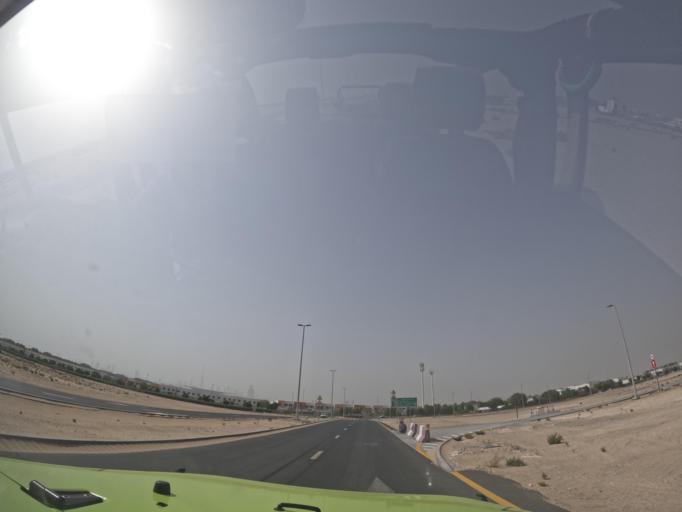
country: AE
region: Dubai
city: Dubai
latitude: 25.1395
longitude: 55.3130
